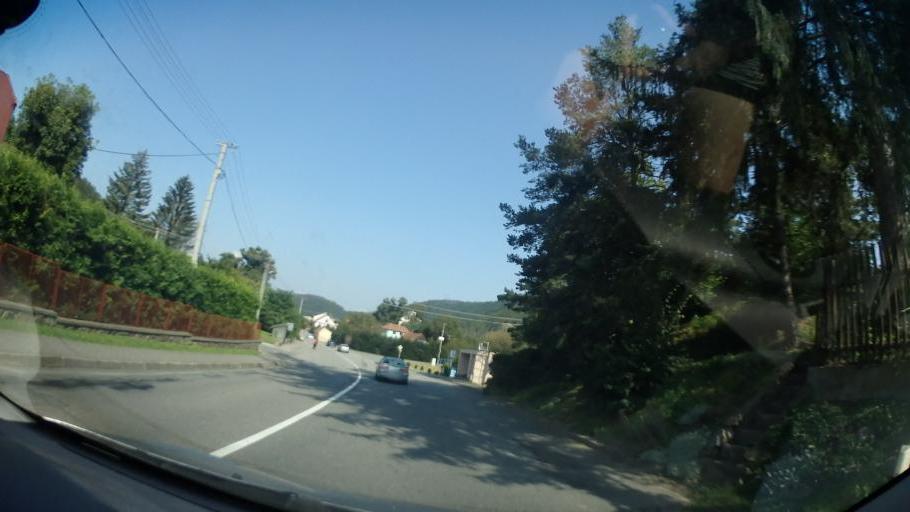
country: CZ
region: South Moravian
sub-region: Okres Brno-Venkov
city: Nedvedice
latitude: 49.4445
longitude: 16.3466
